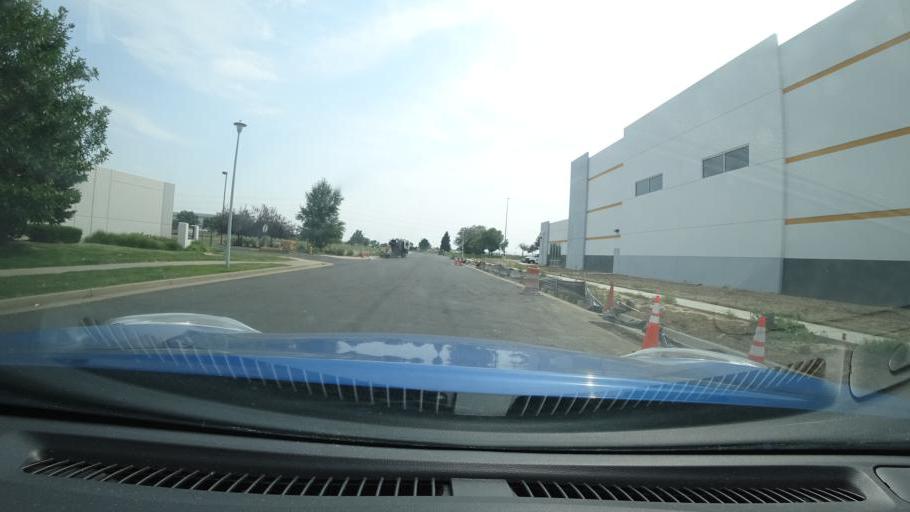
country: US
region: Colorado
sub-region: Adams County
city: Aurora
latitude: 39.7579
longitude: -104.7751
